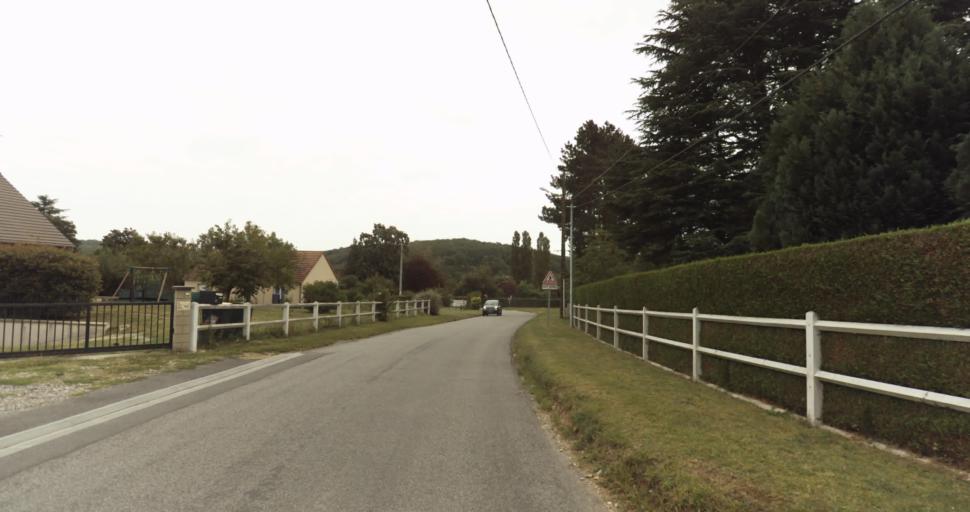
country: FR
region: Haute-Normandie
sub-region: Departement de l'Eure
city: Croth
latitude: 48.8716
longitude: 1.3654
